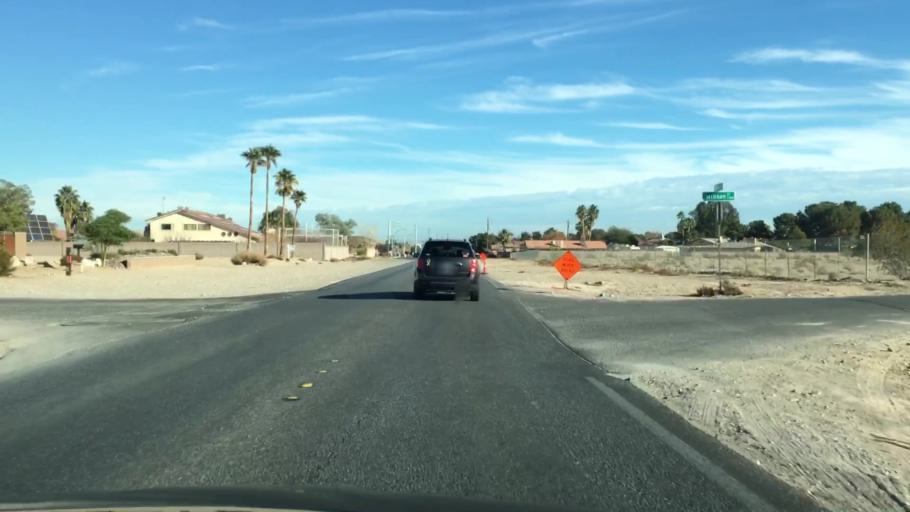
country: US
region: Nevada
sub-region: Clark County
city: Enterprise
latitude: 36.0572
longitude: -115.1950
